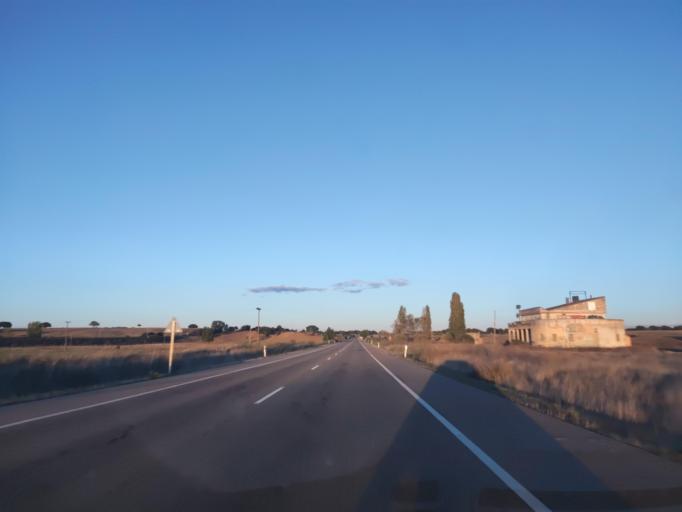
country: ES
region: Castille and Leon
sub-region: Provincia de Salamanca
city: Martin de Yeltes
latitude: 40.7771
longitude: -6.2804
